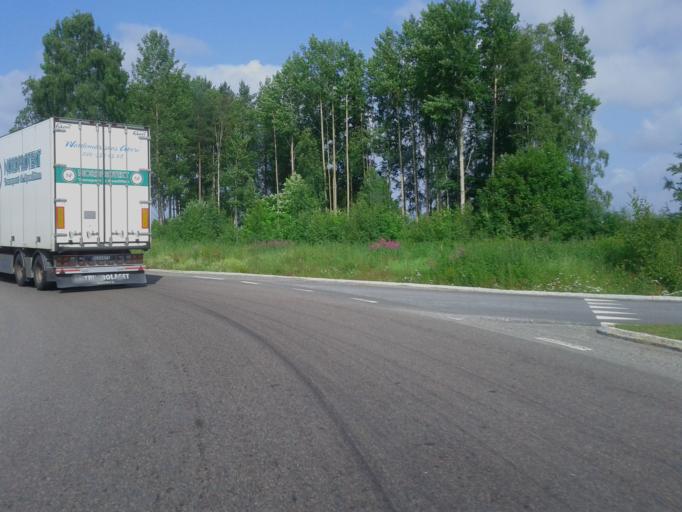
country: SE
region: Vaesterbotten
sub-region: Skelleftea Kommun
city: Skelleftea
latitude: 64.7305
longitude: 20.9763
